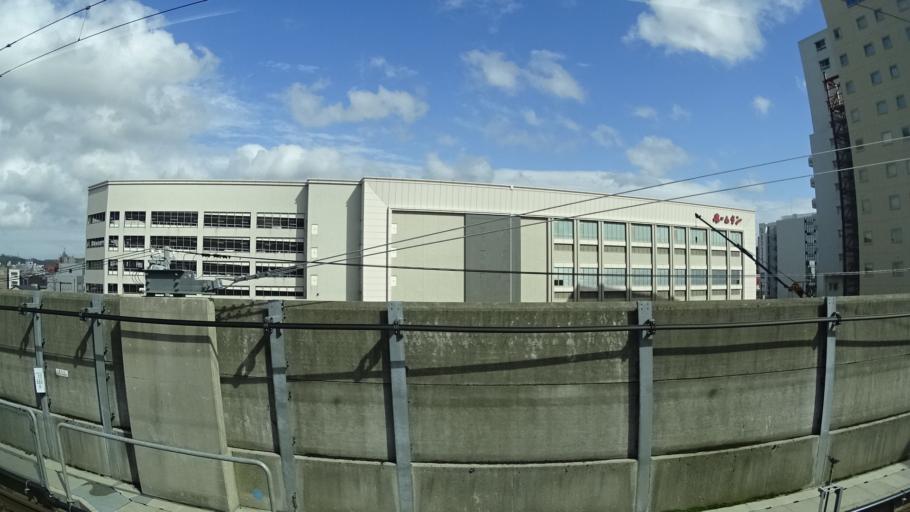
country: JP
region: Ishikawa
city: Kanazawa-shi
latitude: 36.5808
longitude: 136.6505
